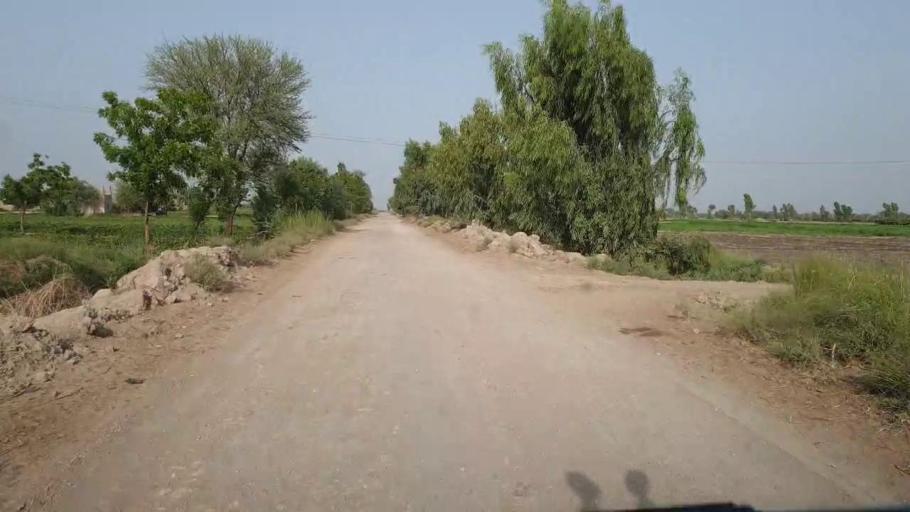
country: PK
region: Sindh
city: Daur
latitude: 26.3407
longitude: 68.2003
